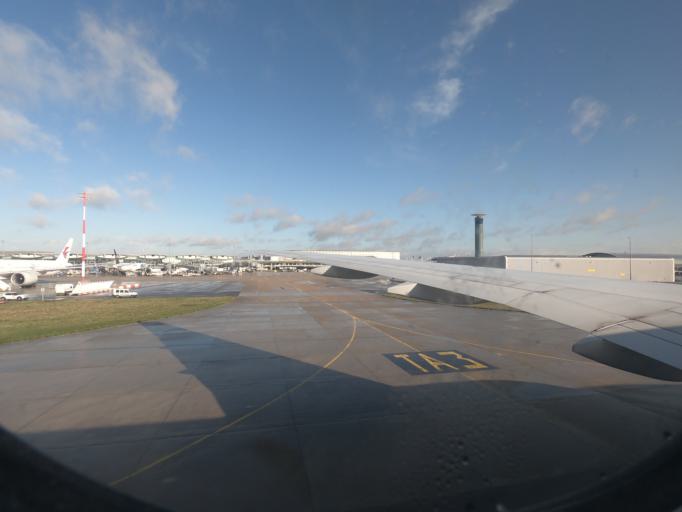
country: FR
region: Ile-de-France
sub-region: Departement de Seine-et-Marne
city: Mitry-Mory
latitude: 48.9995
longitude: 2.5699
